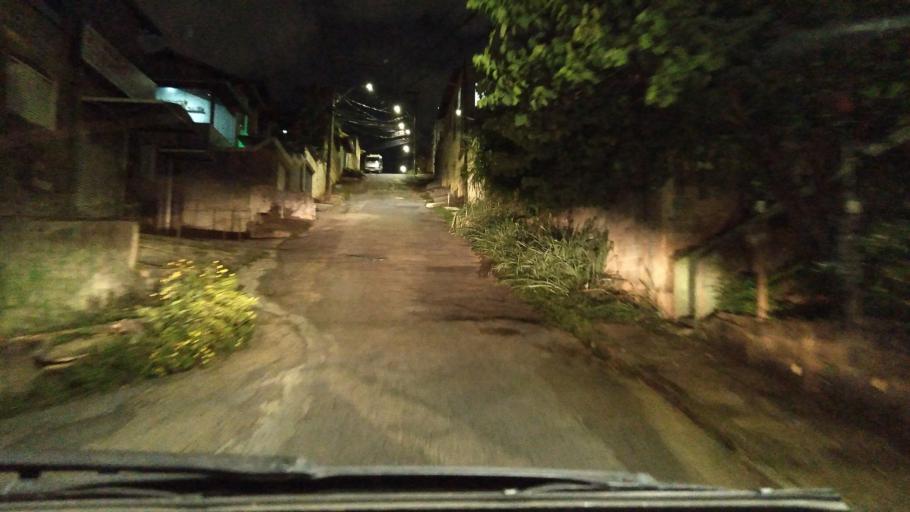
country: BR
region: Minas Gerais
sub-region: Belo Horizonte
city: Belo Horizonte
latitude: -19.8991
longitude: -43.9729
